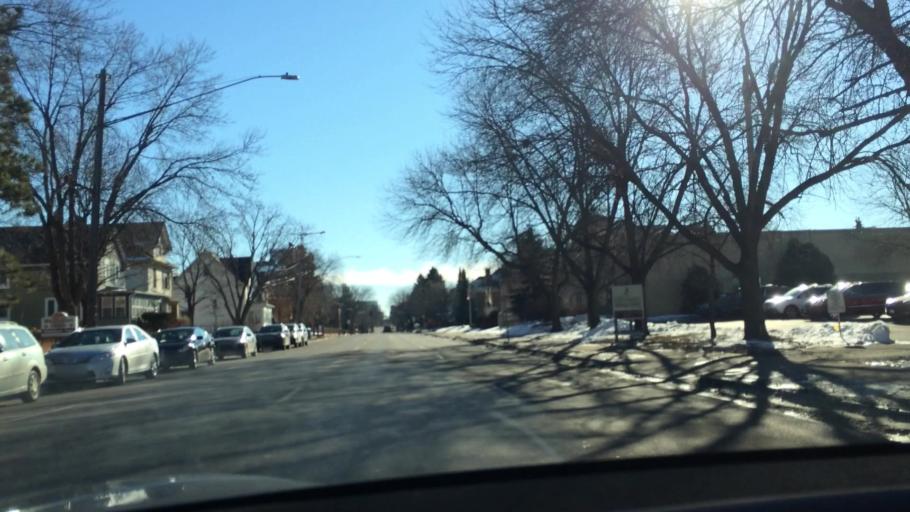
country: US
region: Minnesota
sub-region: Hennepin County
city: Minneapolis
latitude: 44.9955
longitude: -93.2616
